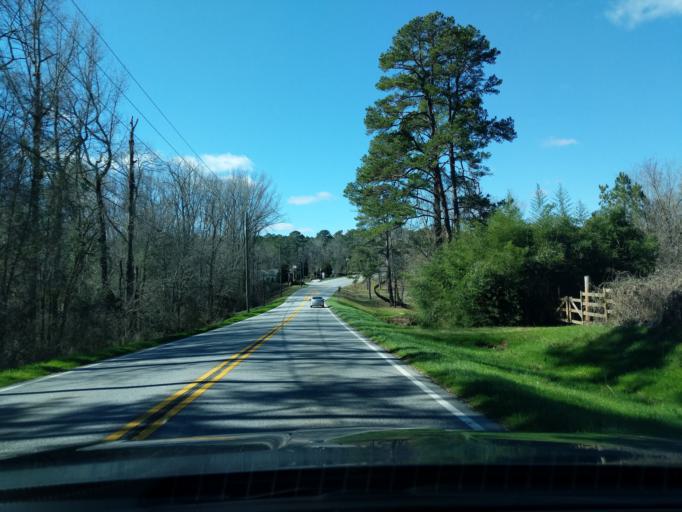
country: US
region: Georgia
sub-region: Columbia County
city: Evans
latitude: 33.5282
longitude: -82.1853
